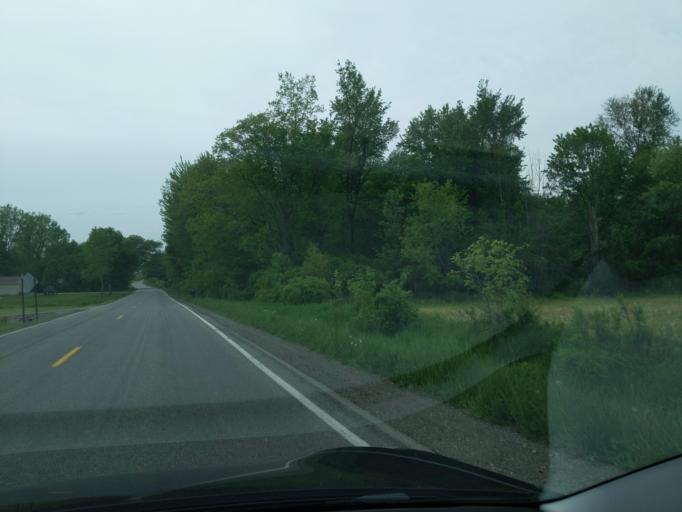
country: US
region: Michigan
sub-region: Ingham County
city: Leslie
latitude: 42.4482
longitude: -84.3577
